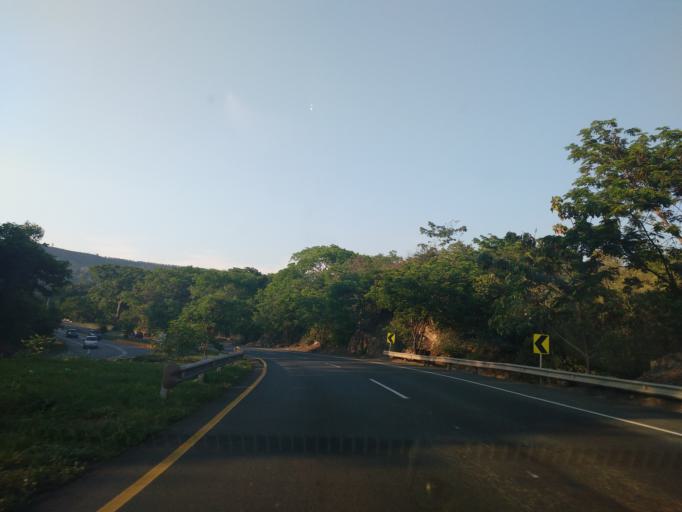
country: CO
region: Tolima
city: Melgar
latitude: 4.2381
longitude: -74.6179
